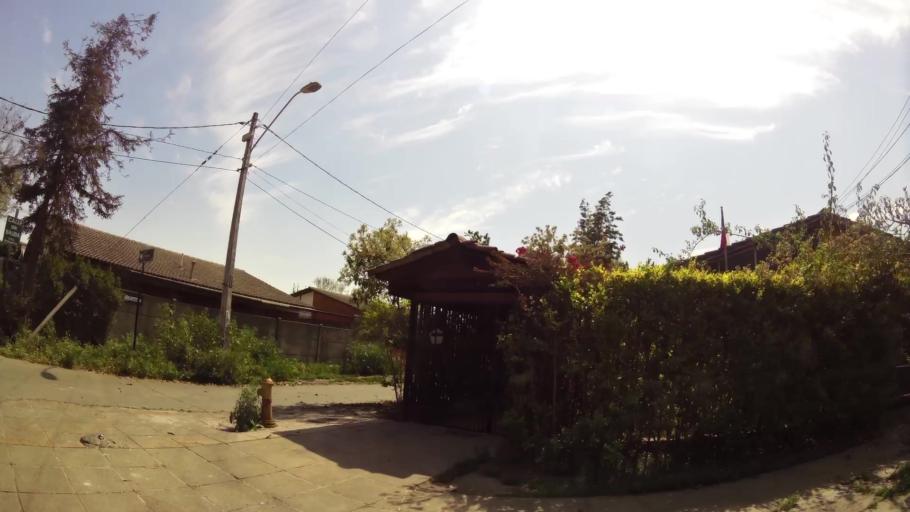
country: CL
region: Santiago Metropolitan
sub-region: Provincia de Santiago
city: La Pintana
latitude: -33.5523
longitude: -70.6641
